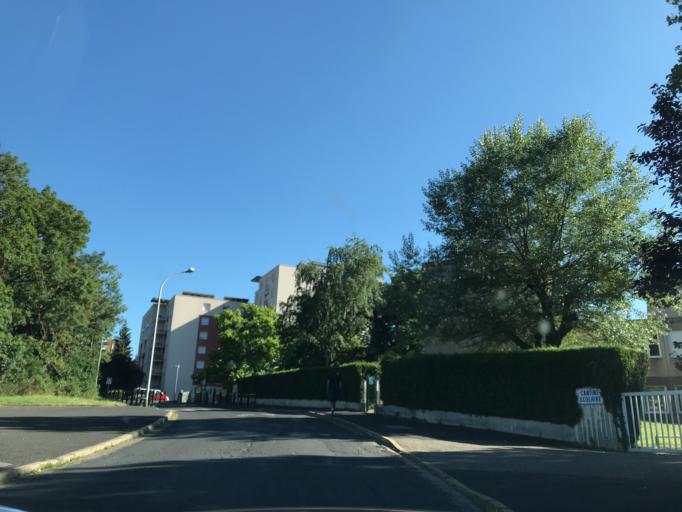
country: FR
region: Auvergne
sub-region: Departement du Puy-de-Dome
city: Thiers
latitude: 45.8471
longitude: 3.5330
